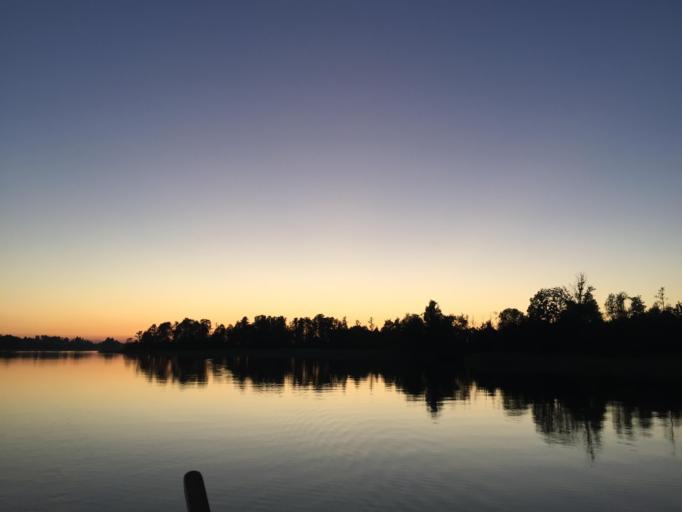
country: LV
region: Rezekne
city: Rezekne
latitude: 56.3585
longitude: 27.4317
